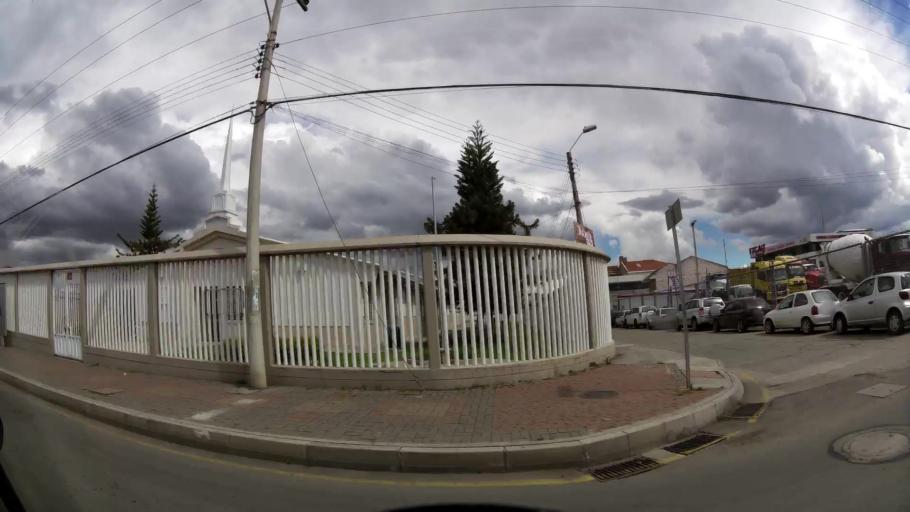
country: EC
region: Azuay
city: Cuenca
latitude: -2.8847
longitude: -78.9822
